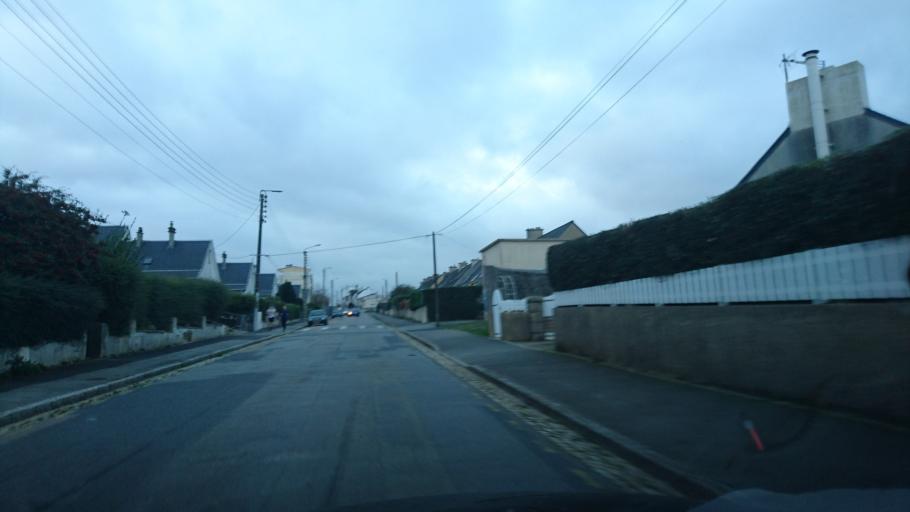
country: FR
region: Brittany
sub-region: Departement du Finistere
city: Brest
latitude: 48.3907
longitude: -4.4641
